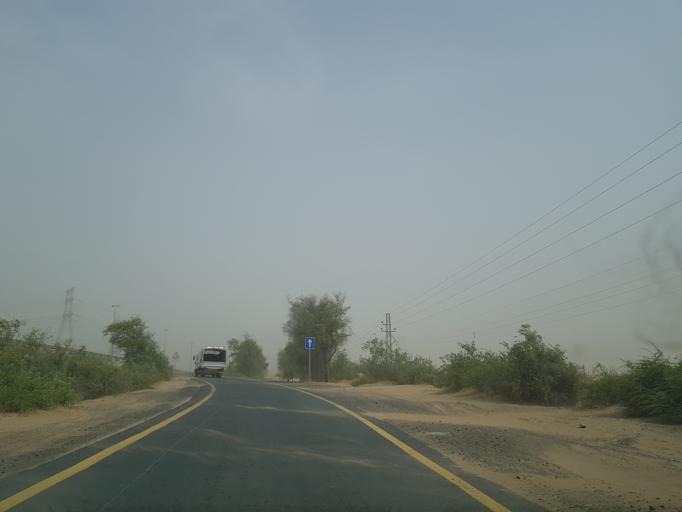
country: AE
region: Dubai
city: Dubai
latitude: 24.9210
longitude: 55.5234
